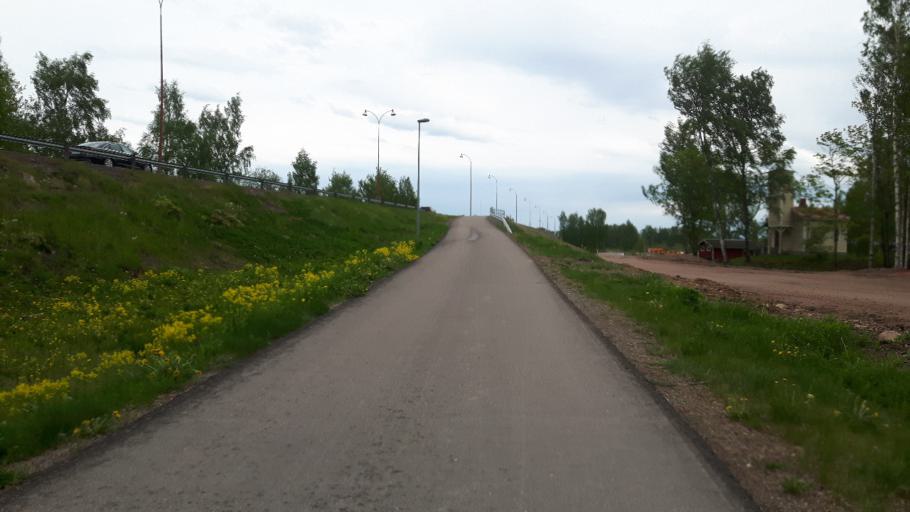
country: FI
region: Kymenlaakso
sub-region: Kotka-Hamina
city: Hamina
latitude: 60.5635
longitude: 27.1768
